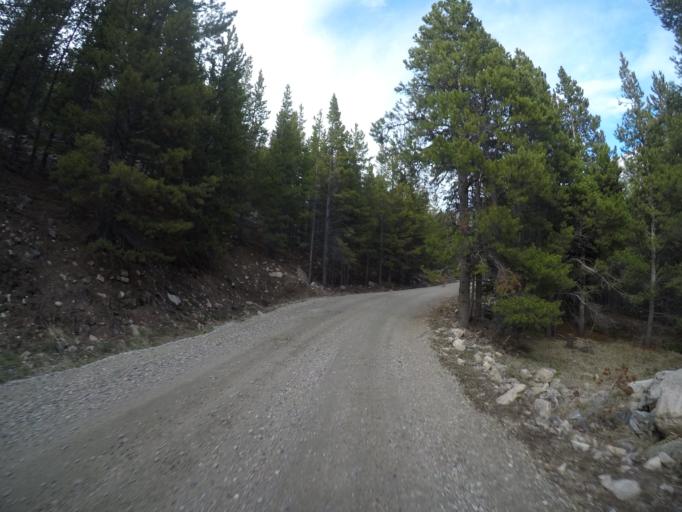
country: US
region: Montana
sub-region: Carbon County
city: Red Lodge
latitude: 45.0247
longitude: -109.4467
